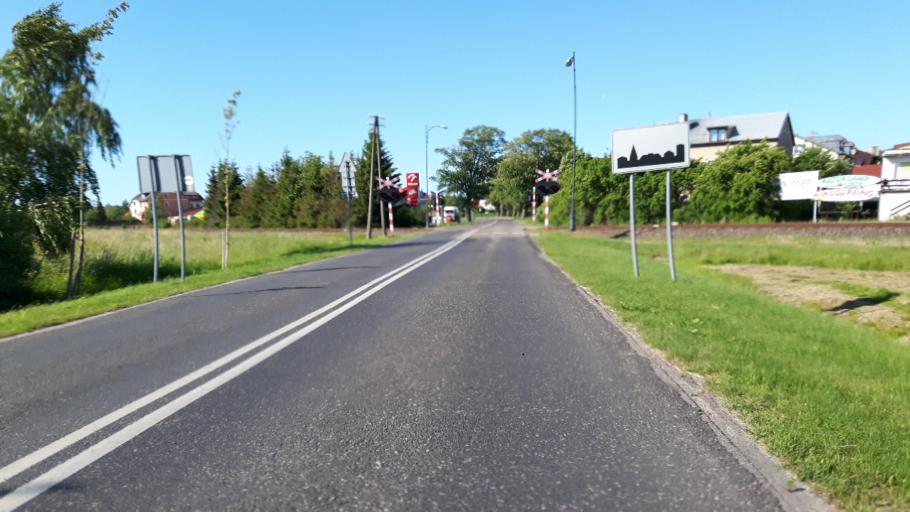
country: PL
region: Pomeranian Voivodeship
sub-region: Powiat leborski
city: Leba
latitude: 54.7503
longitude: 17.5578
